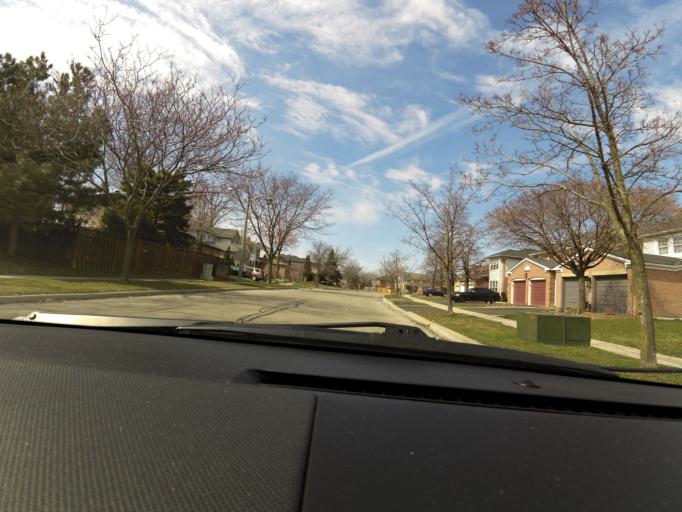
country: CA
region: Ontario
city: Burlington
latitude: 43.3852
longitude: -79.8037
